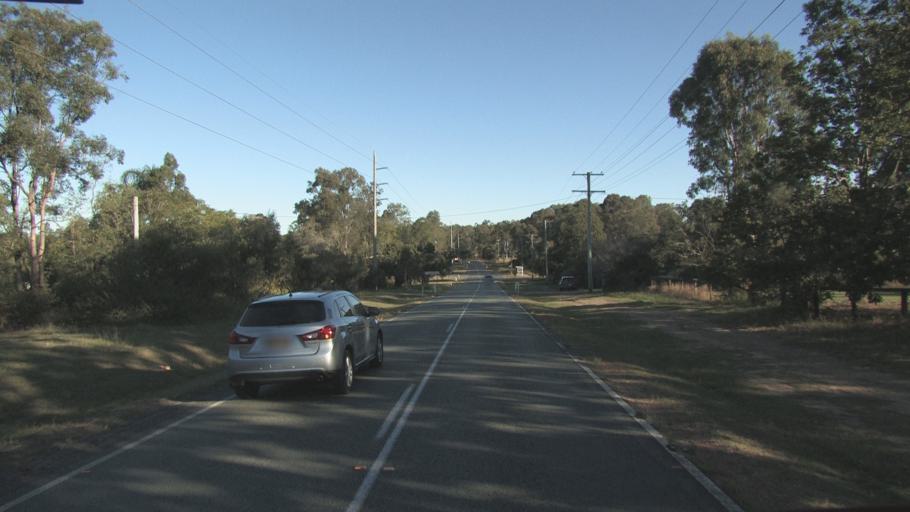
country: AU
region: Queensland
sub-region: Logan
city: Logan Reserve
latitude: -27.7371
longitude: 153.0876
